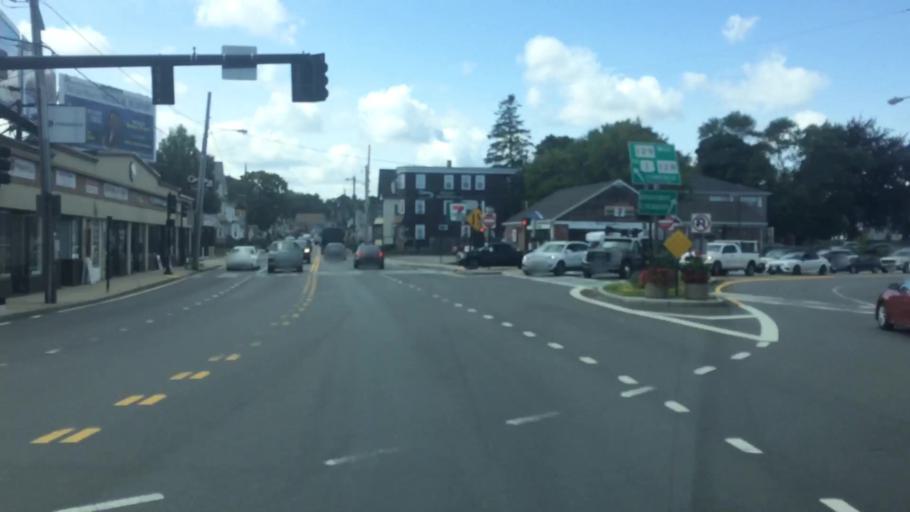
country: US
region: Massachusetts
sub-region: Essex County
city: Lynn
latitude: 42.4850
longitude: -70.9601
